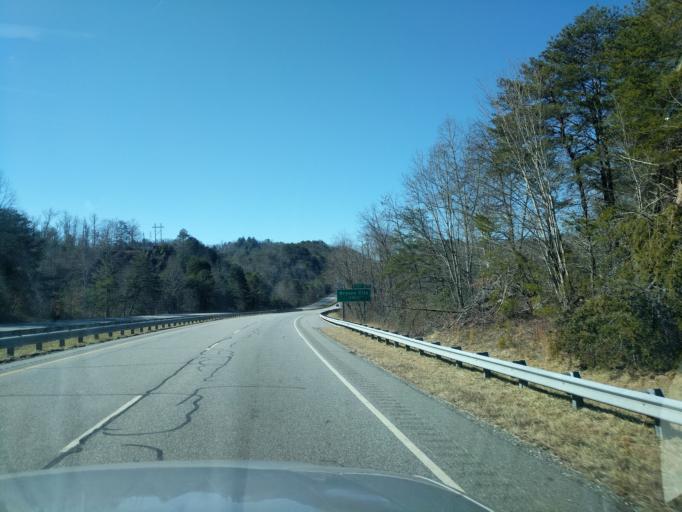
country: US
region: North Carolina
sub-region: Swain County
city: Bryson City
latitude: 35.4255
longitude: -83.4171
